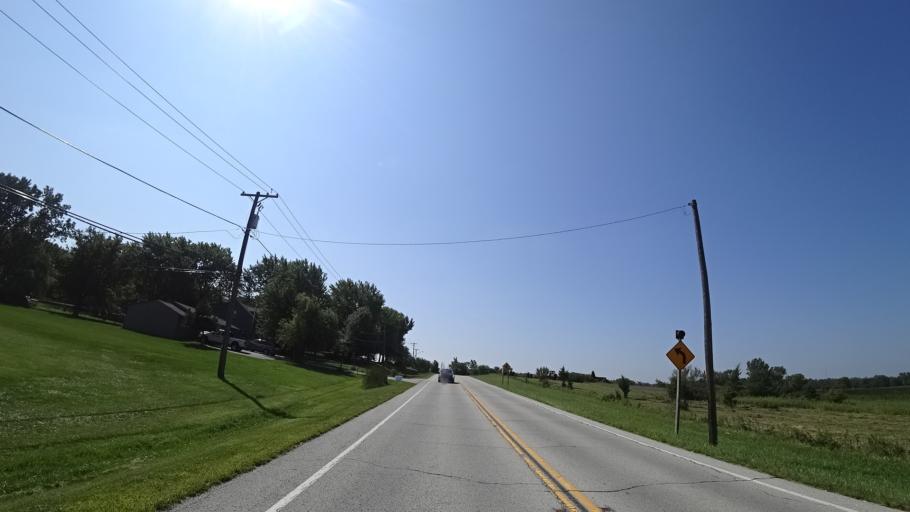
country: US
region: Illinois
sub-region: Cook County
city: Tinley Park
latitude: 41.5715
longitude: -87.7550
